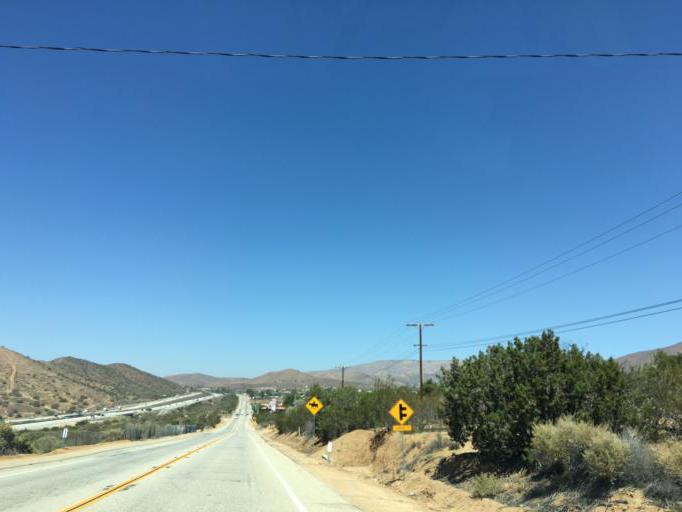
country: US
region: California
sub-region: Los Angeles County
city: Vincent
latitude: 34.4873
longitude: -118.1563
